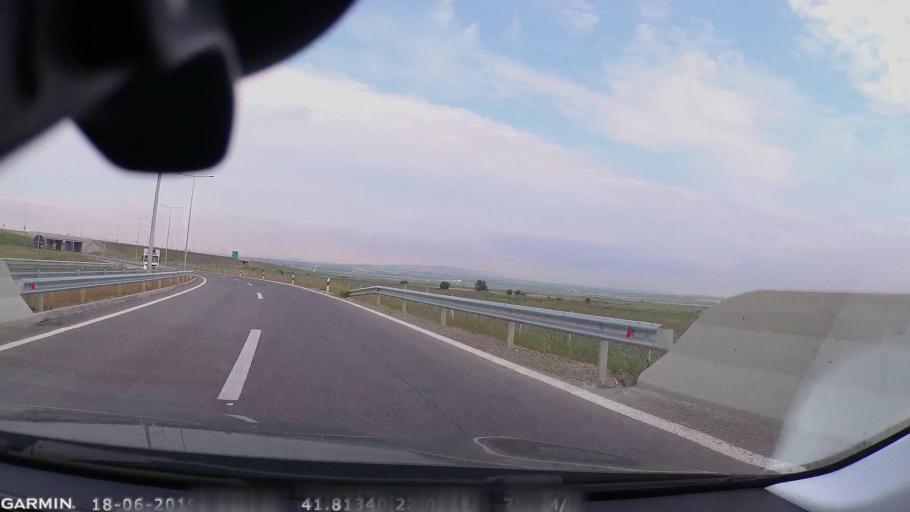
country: MK
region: Sveti Nikole
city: Sveti Nikole
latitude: 41.8131
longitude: 22.0356
